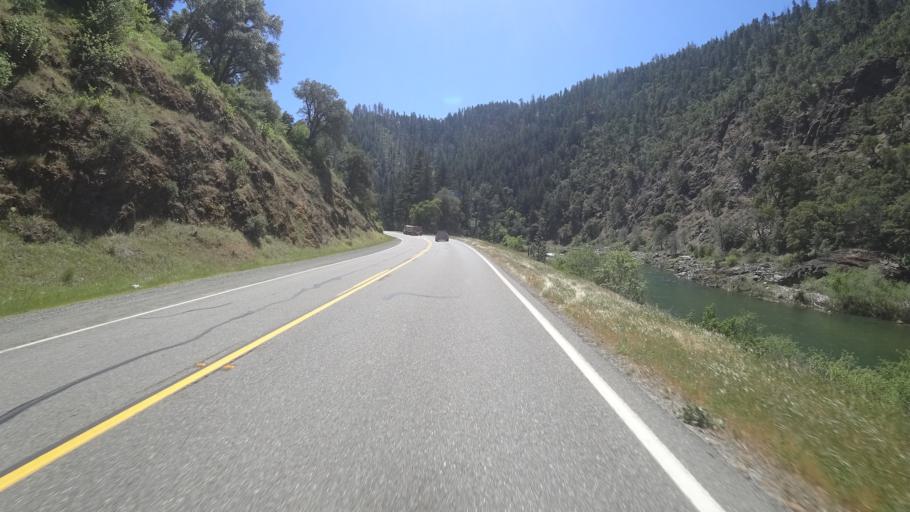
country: US
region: California
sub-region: Trinity County
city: Hayfork
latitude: 40.7568
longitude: -123.2828
